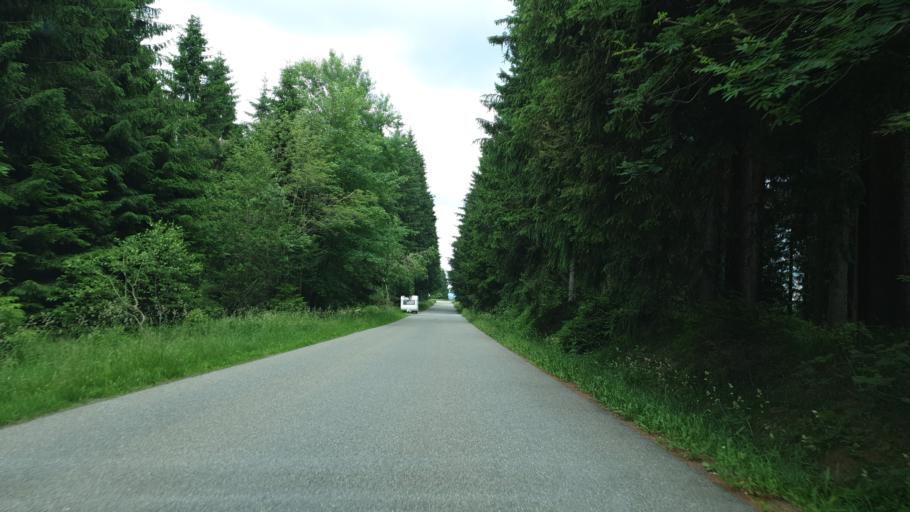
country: DE
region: Saxony
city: Tannenbergsthal
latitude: 50.4155
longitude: 12.4506
